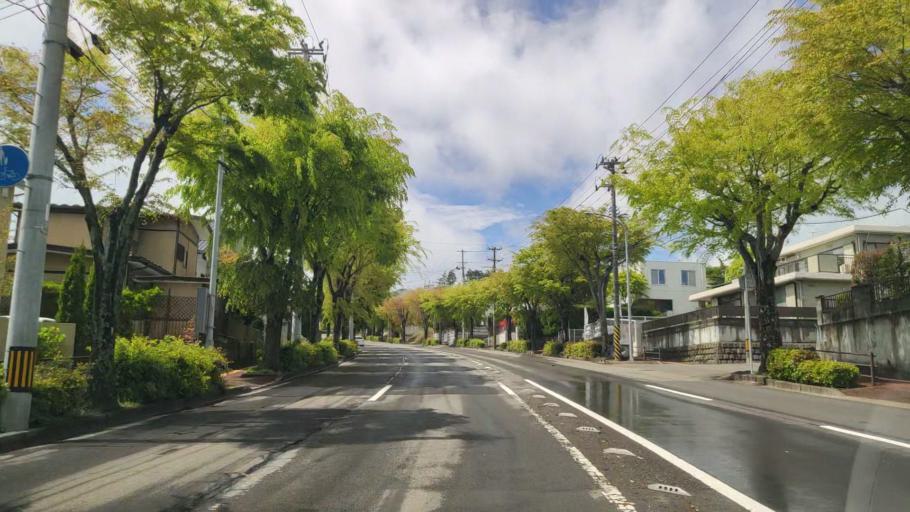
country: JP
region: Miyagi
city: Sendai
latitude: 38.2410
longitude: 140.8448
